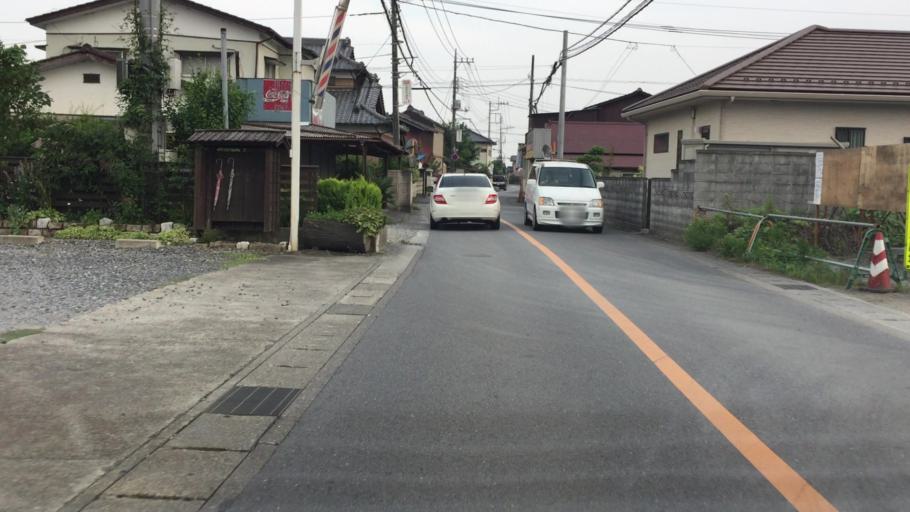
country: JP
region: Tochigi
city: Tochigi
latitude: 36.3977
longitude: 139.7180
